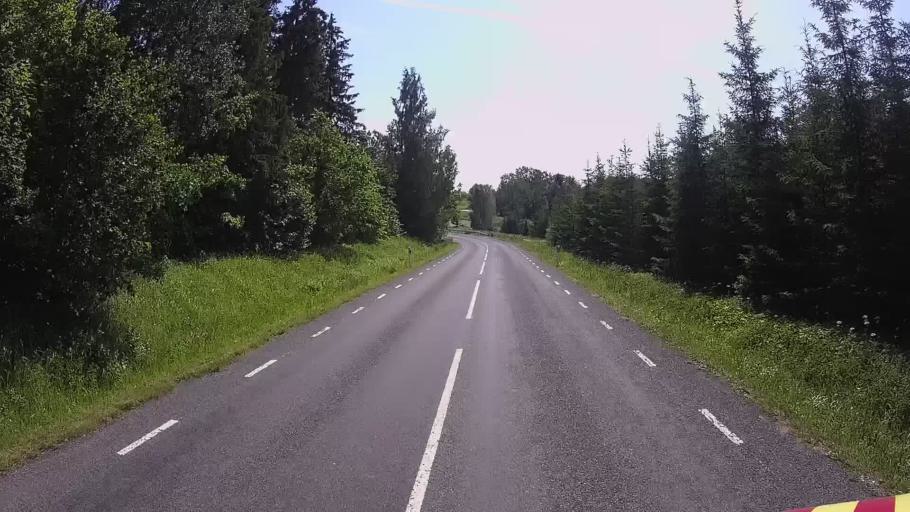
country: EE
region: Viljandimaa
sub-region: Karksi vald
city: Karksi-Nuia
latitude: 58.0771
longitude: 25.5605
